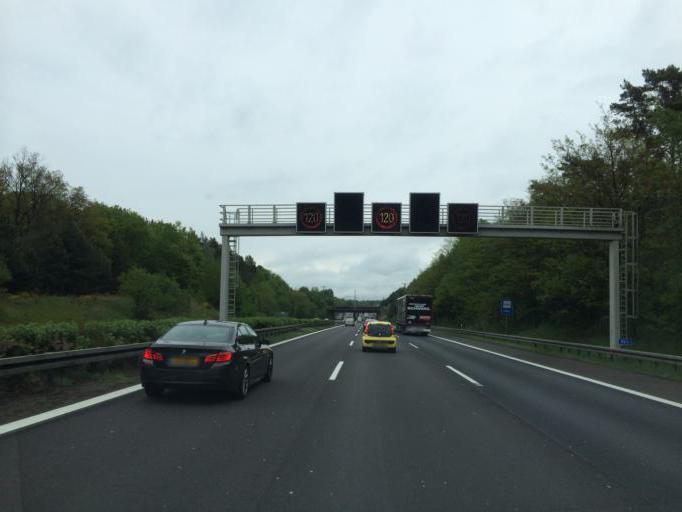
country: DE
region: Brandenburg
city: Michendorf
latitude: 52.3034
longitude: 13.0021
